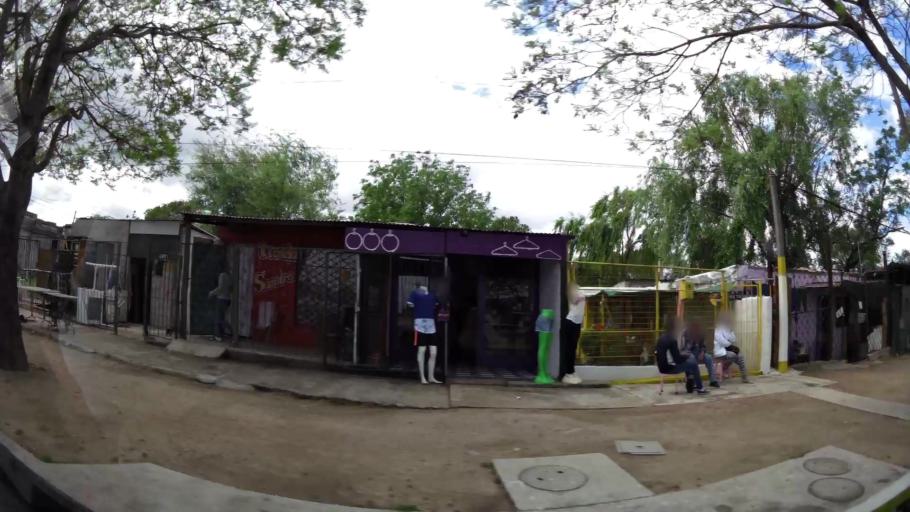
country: UY
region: Montevideo
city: Montevideo
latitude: -34.8499
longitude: -56.1581
